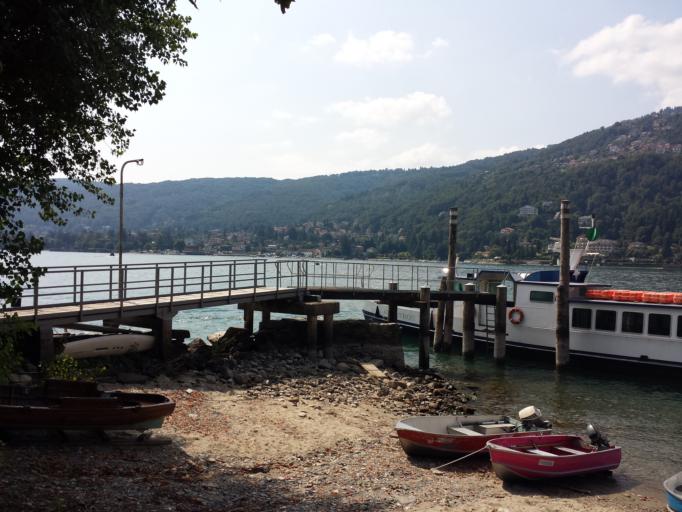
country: IT
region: Piedmont
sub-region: Provincia Verbano-Cusio-Ossola
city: Baveno
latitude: 45.9000
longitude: 8.5211
